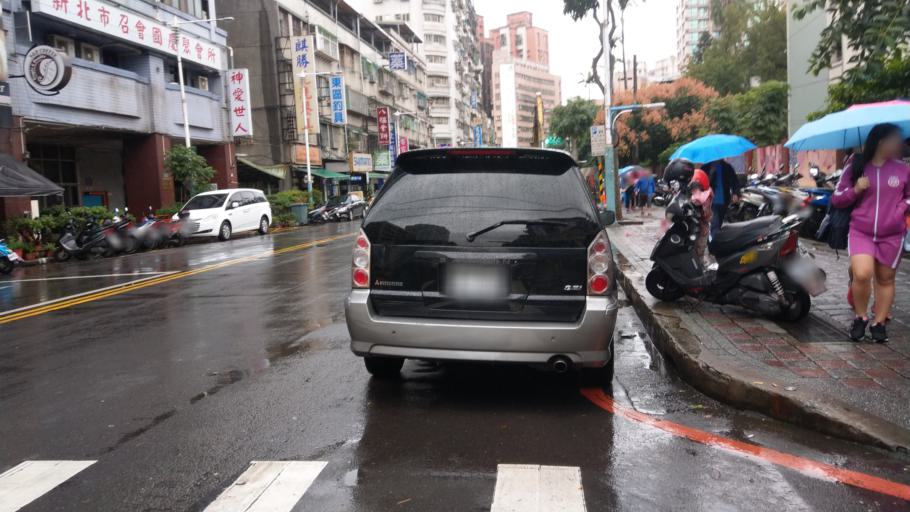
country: TW
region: Taipei
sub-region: Taipei
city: Banqiao
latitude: 24.9990
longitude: 121.4632
